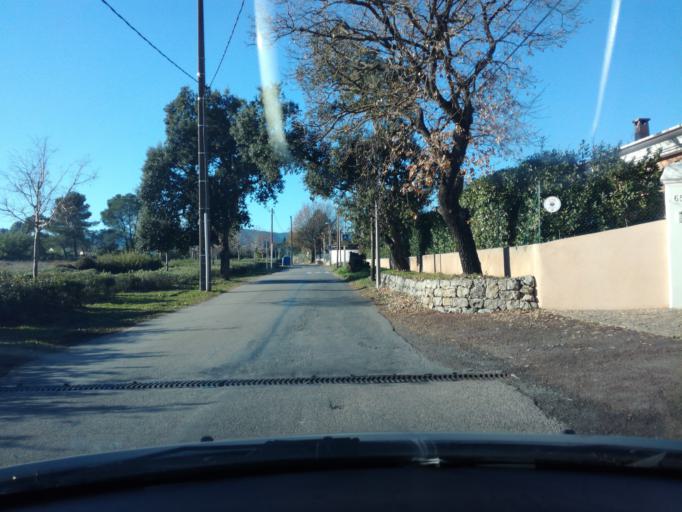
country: FR
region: Provence-Alpes-Cote d'Azur
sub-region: Departement des Alpes-Maritimes
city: La Roquette-sur-Siagne
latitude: 43.6023
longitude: 6.9519
